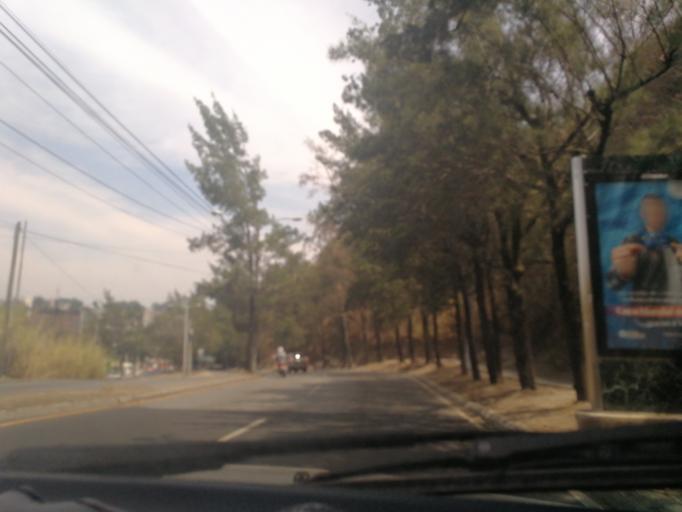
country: GT
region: Guatemala
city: Guatemala City
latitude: 14.6285
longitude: -90.4829
